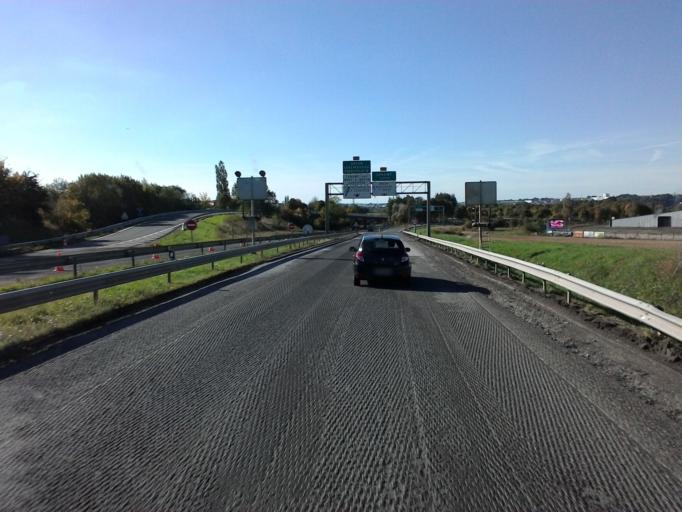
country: FR
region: Lorraine
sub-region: Departement de Meurthe-et-Moselle
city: Mexy
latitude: 49.5023
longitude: 5.7928
